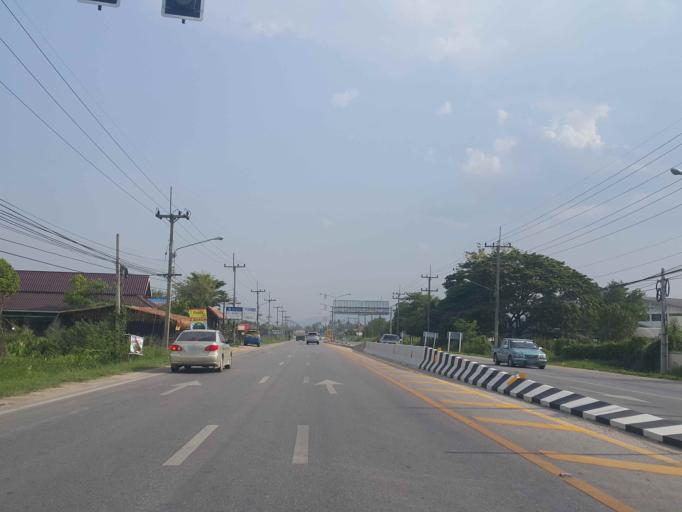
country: TH
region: Chiang Mai
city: Mae Taeng
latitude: 19.0252
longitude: 98.9448
